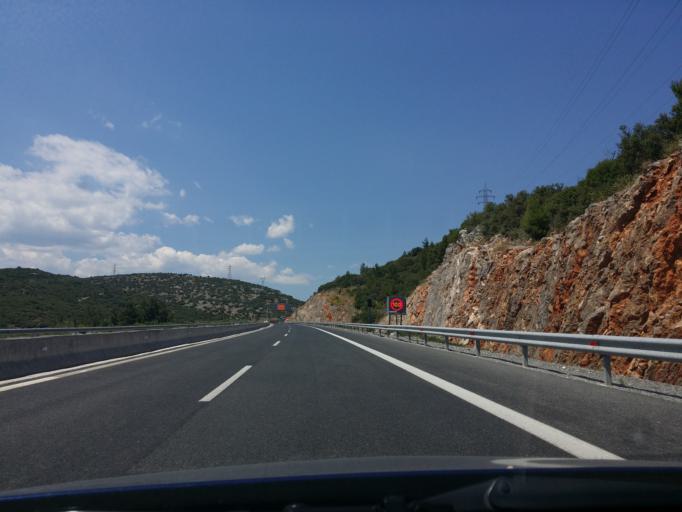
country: GR
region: Peloponnese
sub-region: Nomos Arkadias
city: Tripoli
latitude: 37.4340
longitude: 22.3112
